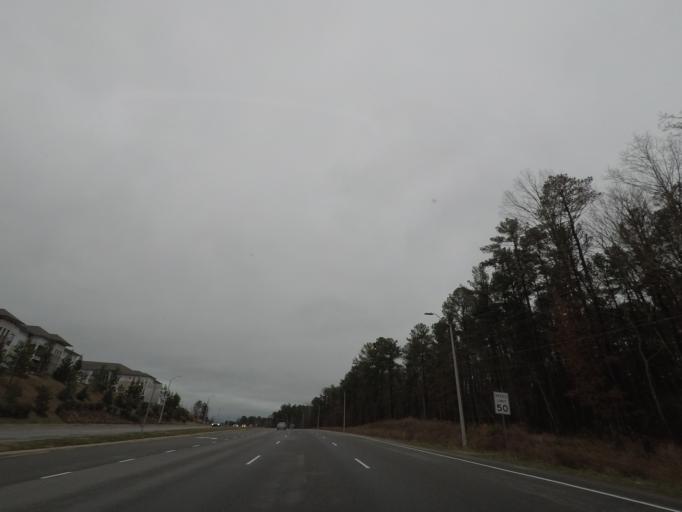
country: US
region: North Carolina
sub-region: Wake County
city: Green Level
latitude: 35.8505
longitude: -78.8940
